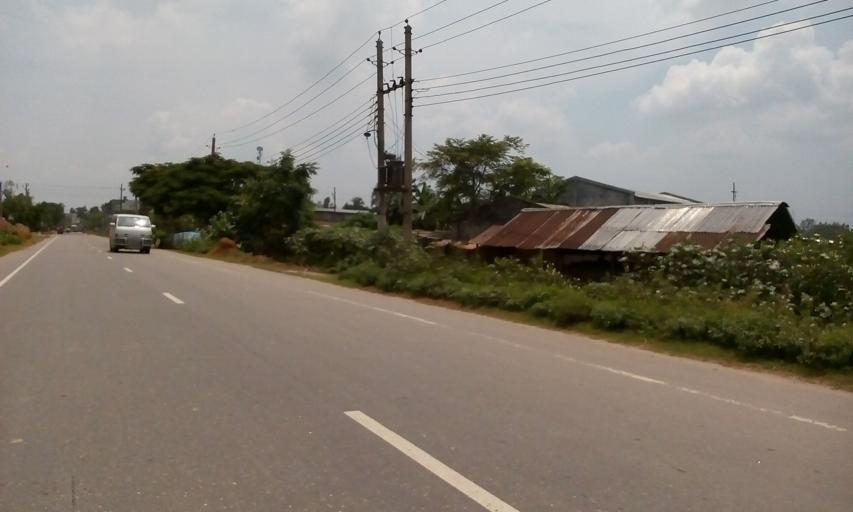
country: BD
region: Rangpur Division
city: Parbatipur
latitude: 25.5027
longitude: 88.9718
